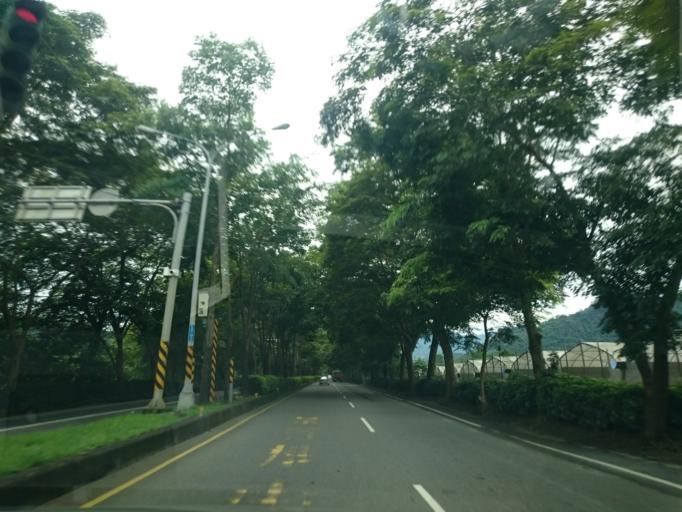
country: TW
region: Taiwan
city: Lugu
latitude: 23.8283
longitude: 120.7524
